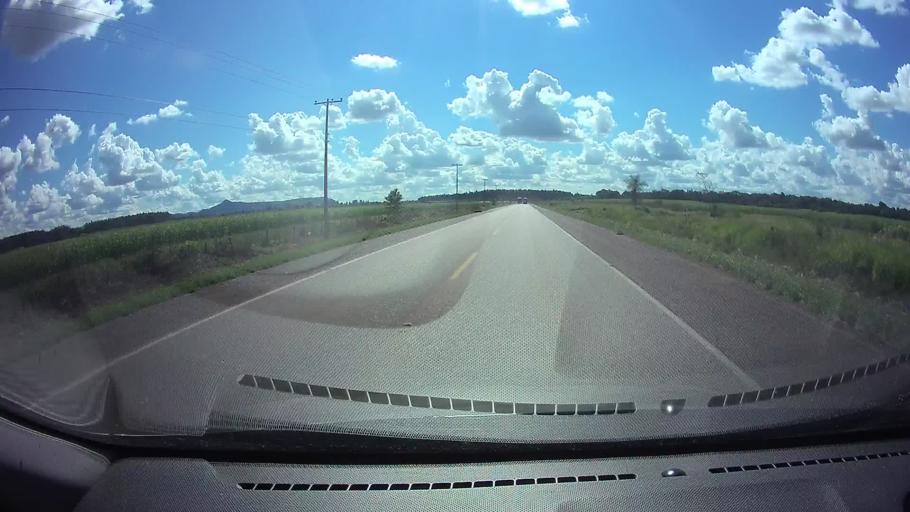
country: PY
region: Guaira
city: Coronel Martinez
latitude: -25.7608
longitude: -56.6955
